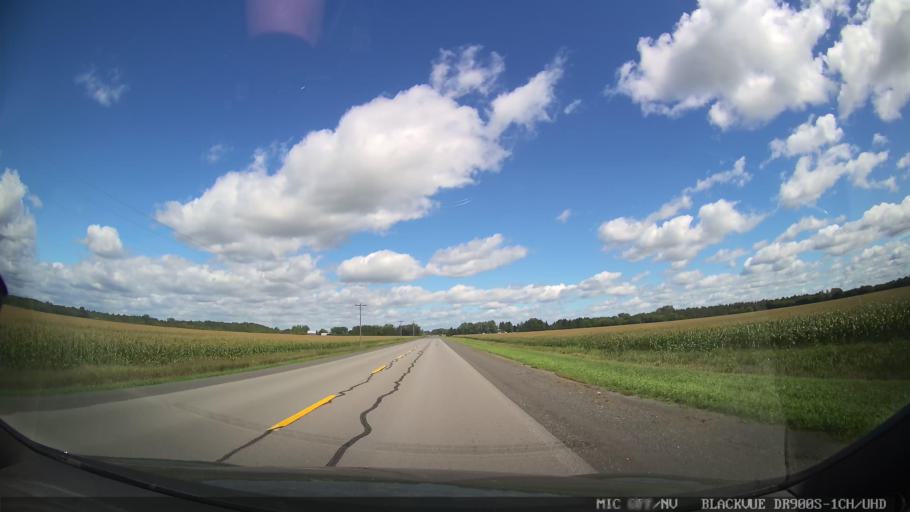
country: CA
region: Ontario
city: Bells Corners
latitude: 45.1801
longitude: -75.7548
